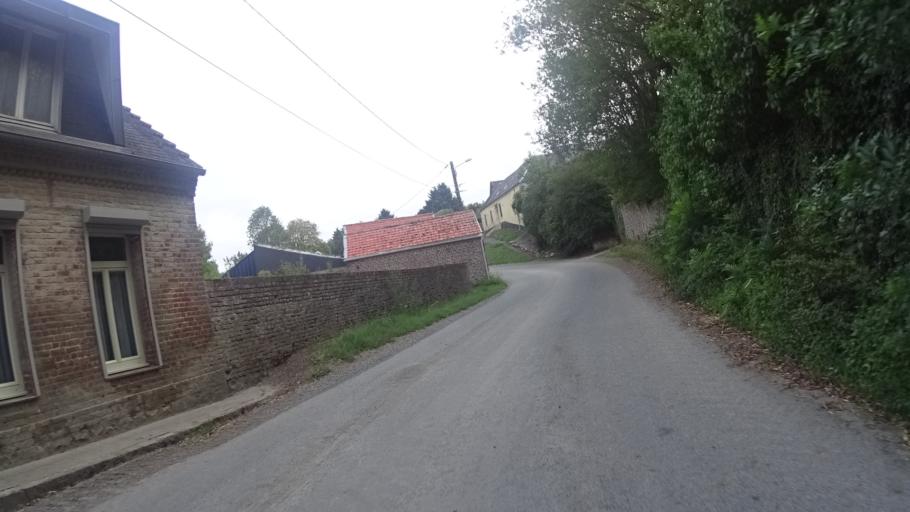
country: FR
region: Picardie
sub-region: Departement de l'Aisne
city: Guise
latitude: 49.9029
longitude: 3.5640
